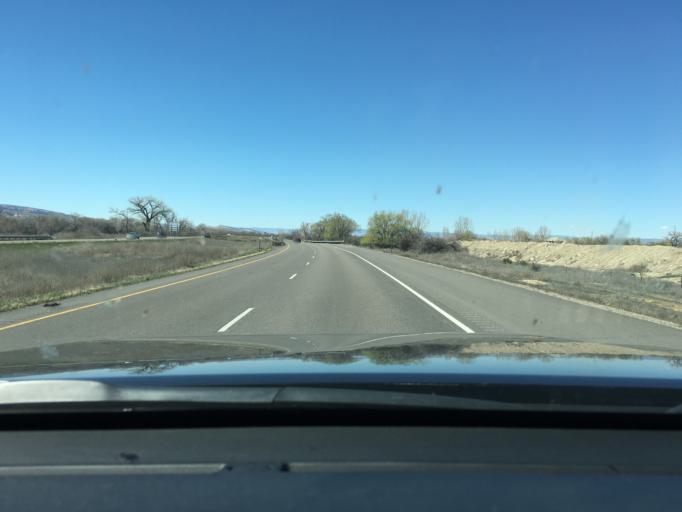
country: US
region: Colorado
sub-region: Mesa County
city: Redlands
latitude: 39.1164
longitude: -108.6663
